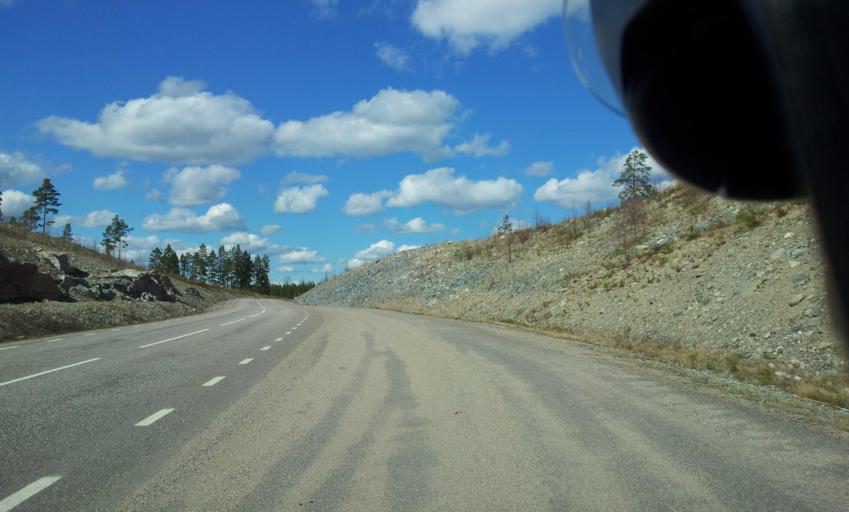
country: SE
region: Gaevleborg
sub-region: Ovanakers Kommun
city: Edsbyn
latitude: 61.2328
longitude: 15.8836
